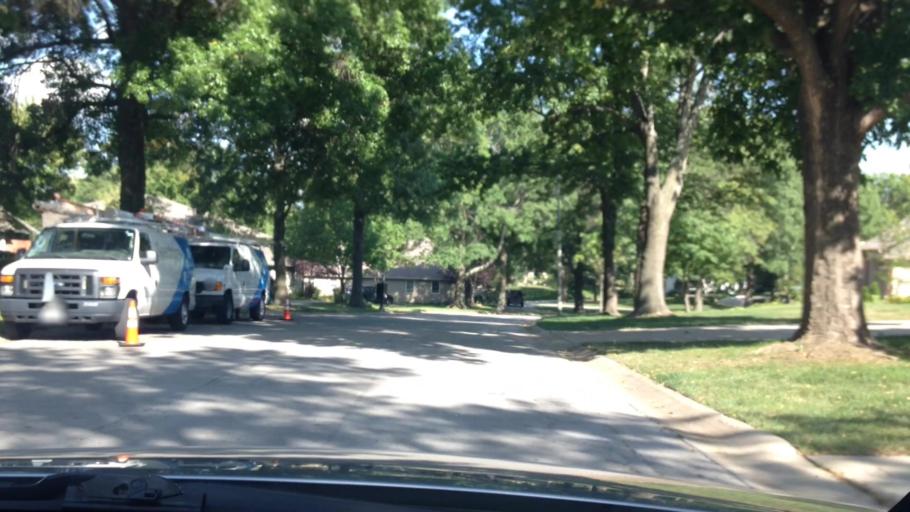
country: US
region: Kansas
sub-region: Johnson County
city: Leawood
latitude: 38.8979
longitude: -94.6116
